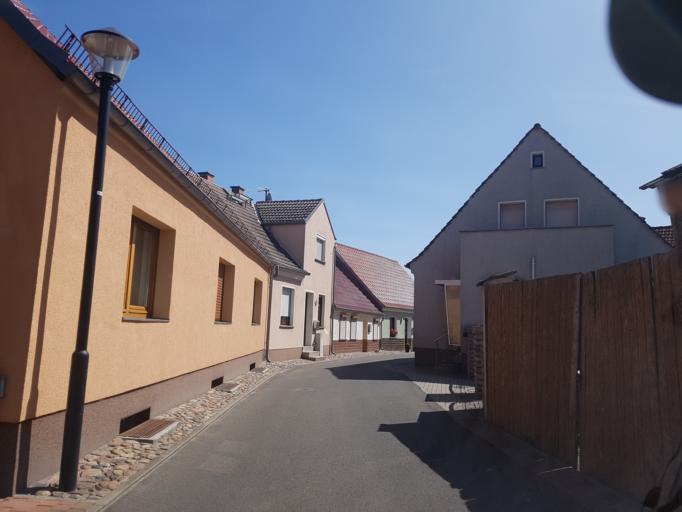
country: DE
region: Brandenburg
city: Niemegk
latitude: 52.0758
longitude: 12.6905
